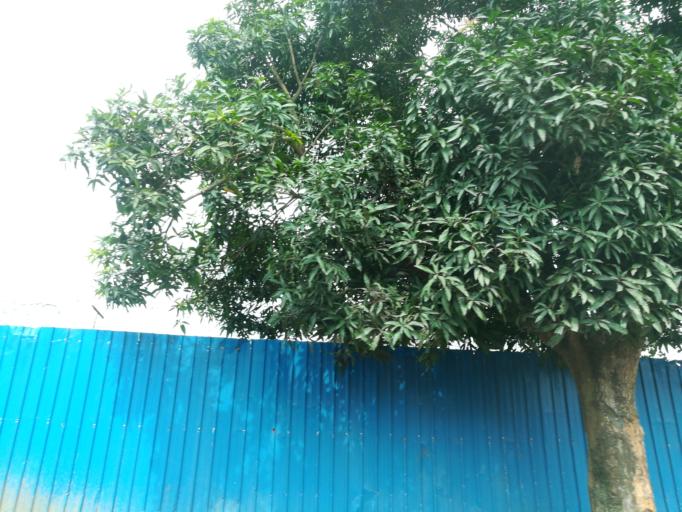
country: NG
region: Lagos
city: Oshodi
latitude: 6.5772
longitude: 3.3253
